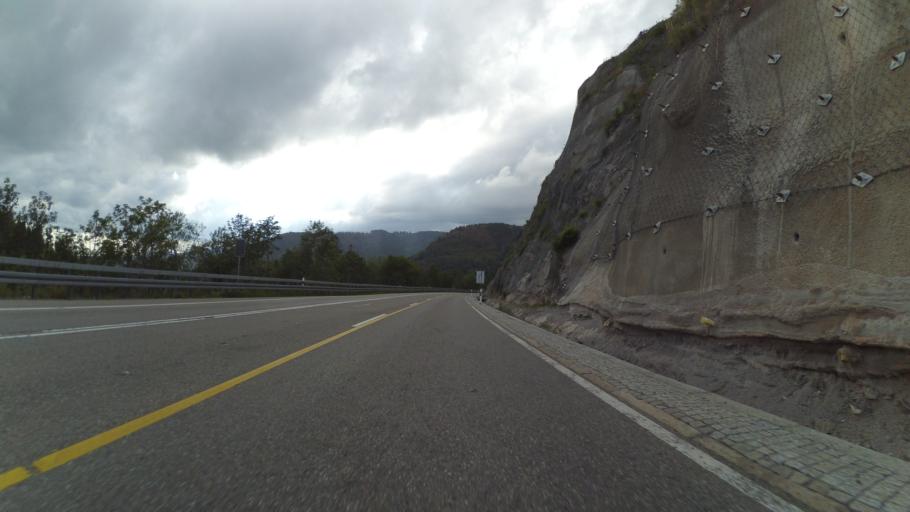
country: DE
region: Baden-Wuerttemberg
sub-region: Freiburg Region
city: Bernau
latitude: 47.8580
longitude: 8.0183
